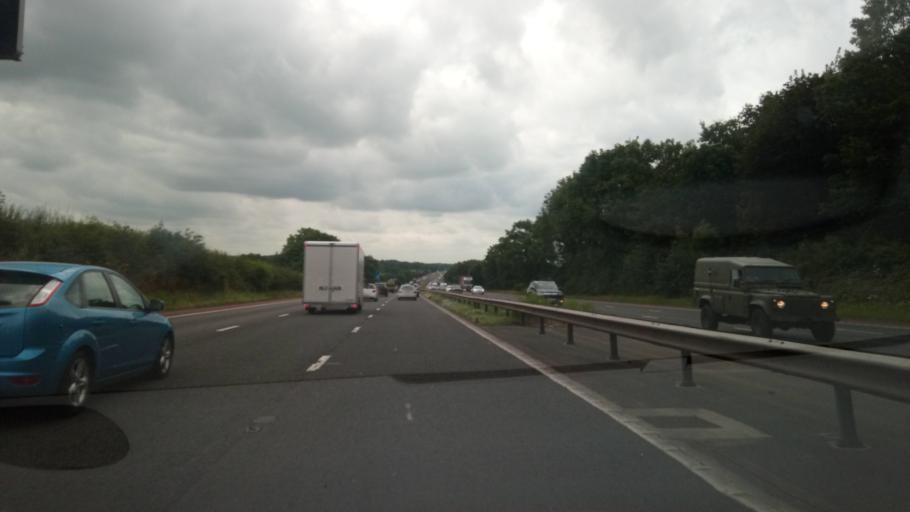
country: GB
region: England
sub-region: Lancashire
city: Galgate
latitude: 54.0080
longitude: -2.7808
